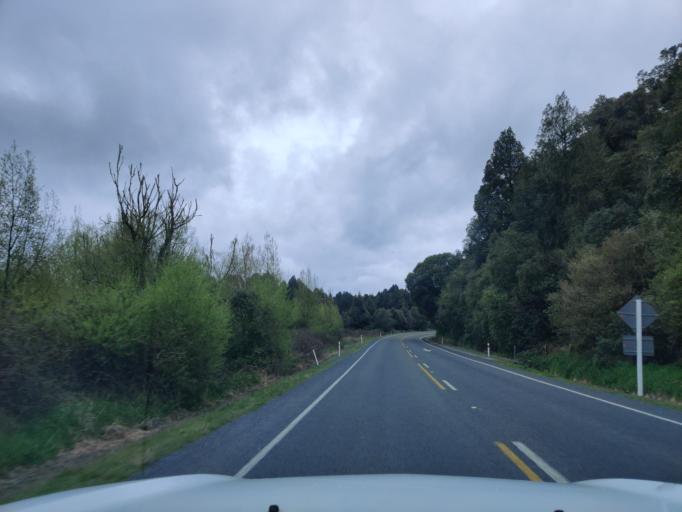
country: NZ
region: Waikato
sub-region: Otorohanga District
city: Otorohanga
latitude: -38.5298
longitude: 175.1768
